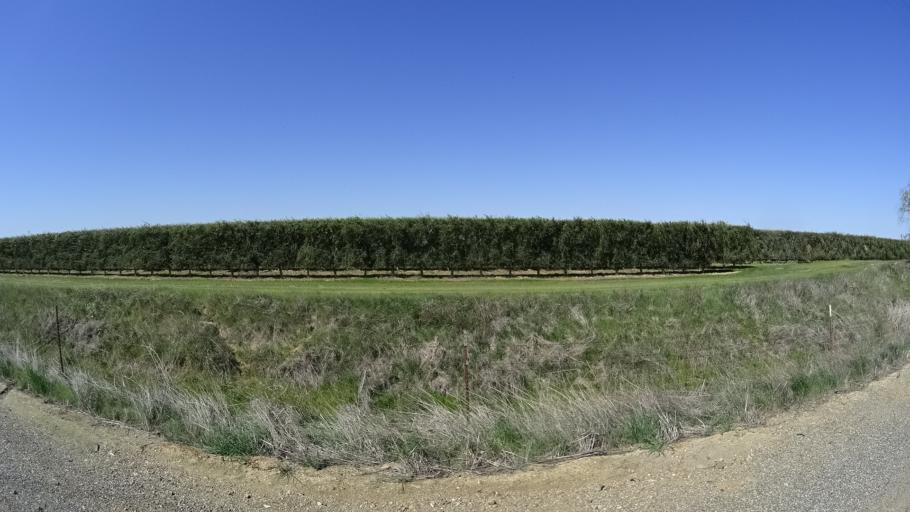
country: US
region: California
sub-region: Glenn County
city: Orland
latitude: 39.6485
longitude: -122.2533
